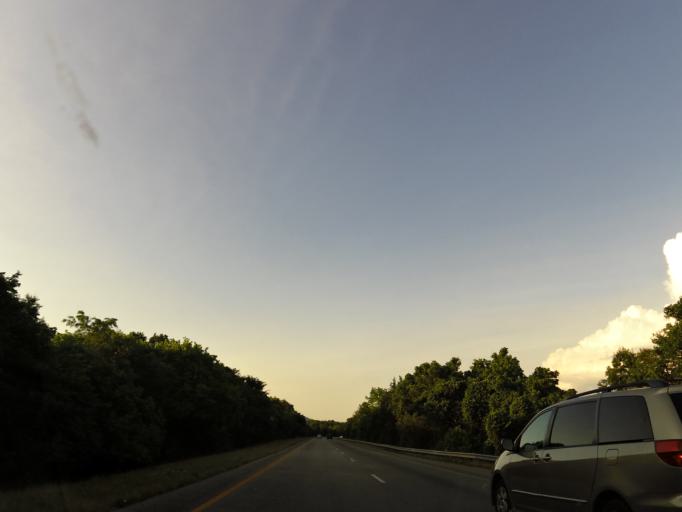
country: US
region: Georgia
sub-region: Dade County
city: Trenton
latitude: 34.8510
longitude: -85.5272
